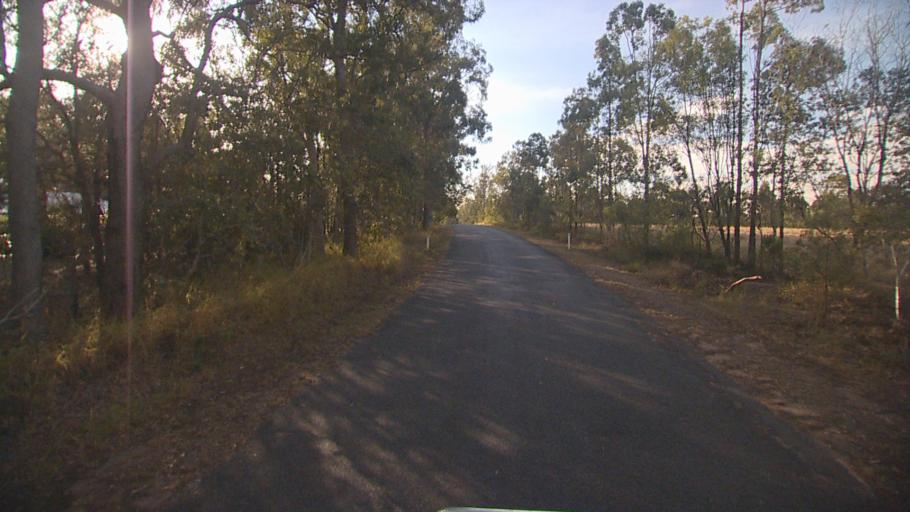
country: AU
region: Queensland
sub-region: Logan
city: Chambers Flat
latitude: -27.8415
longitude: 153.1194
